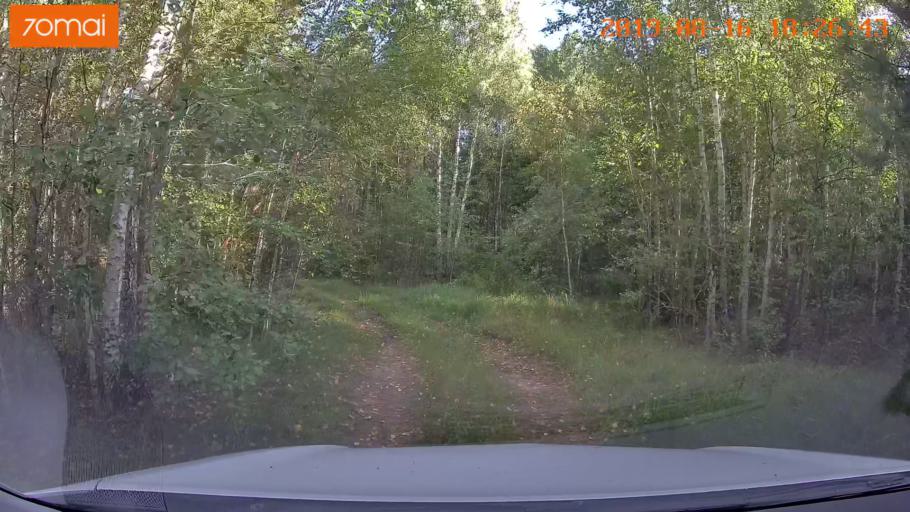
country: BY
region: Mogilev
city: Asipovichy
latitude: 53.2026
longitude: 28.6390
